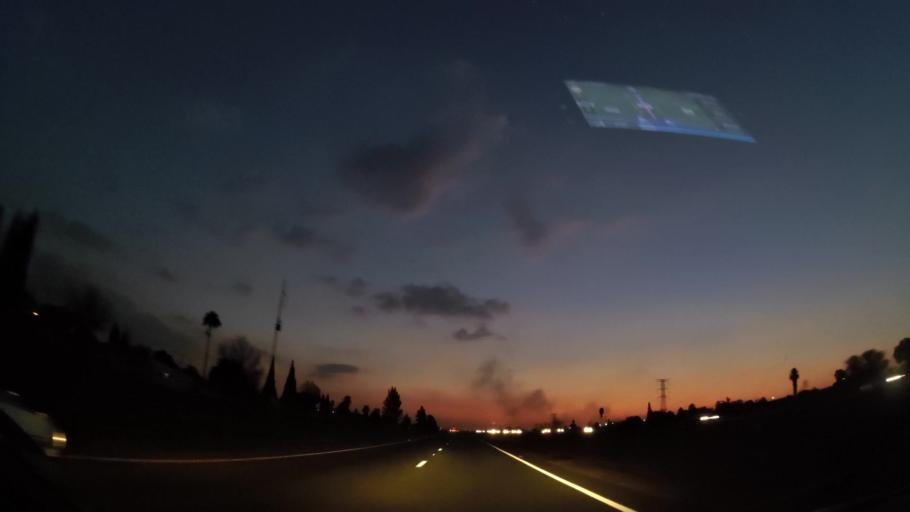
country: ZA
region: Gauteng
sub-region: Ekurhuleni Metropolitan Municipality
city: Boksburg
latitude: -26.2521
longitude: 28.2980
